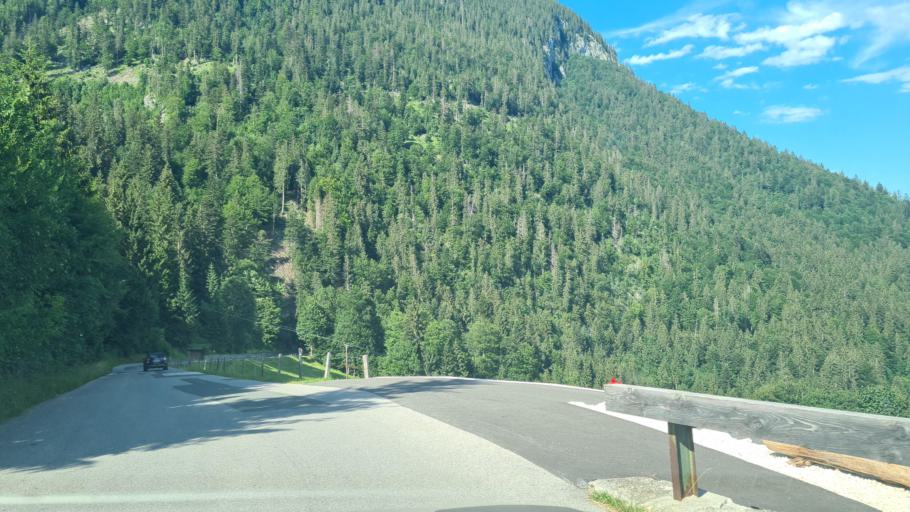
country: AT
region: Salzburg
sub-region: Politischer Bezirk Zell am See
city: Unken
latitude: 47.6507
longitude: 12.6839
